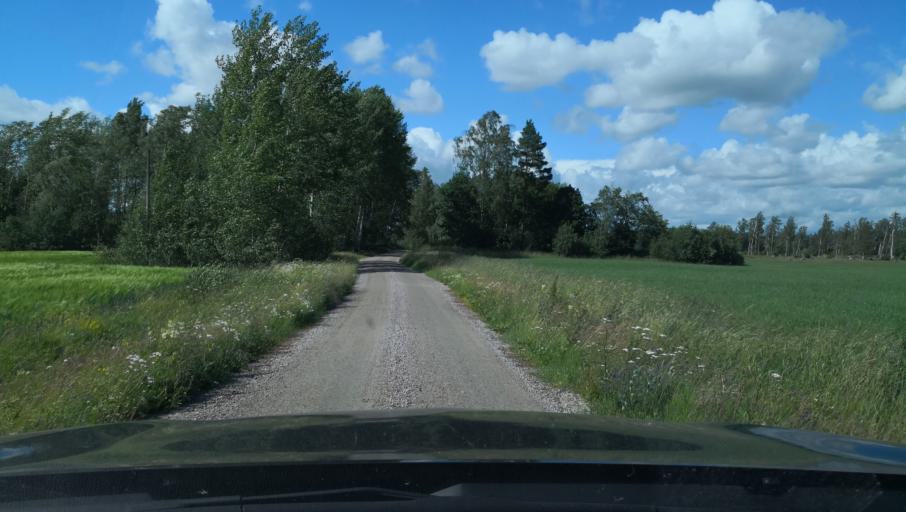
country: SE
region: Vaestmanland
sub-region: Kungsors Kommun
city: Kungsoer
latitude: 59.3195
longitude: 16.0517
